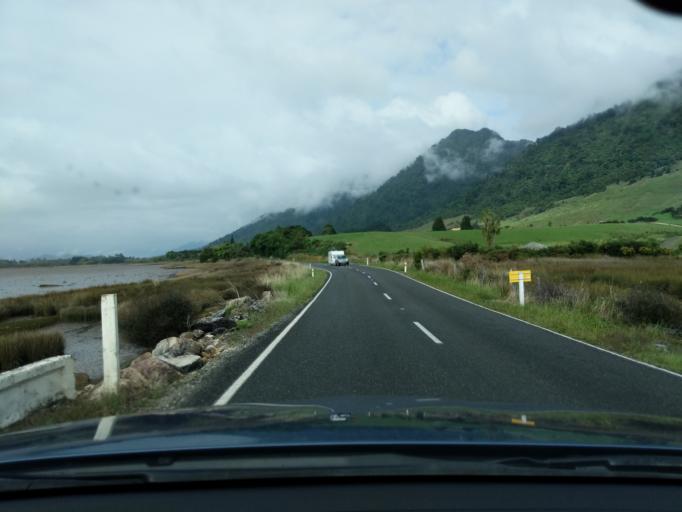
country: NZ
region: Tasman
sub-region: Tasman District
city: Takaka
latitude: -40.6442
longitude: 172.6619
